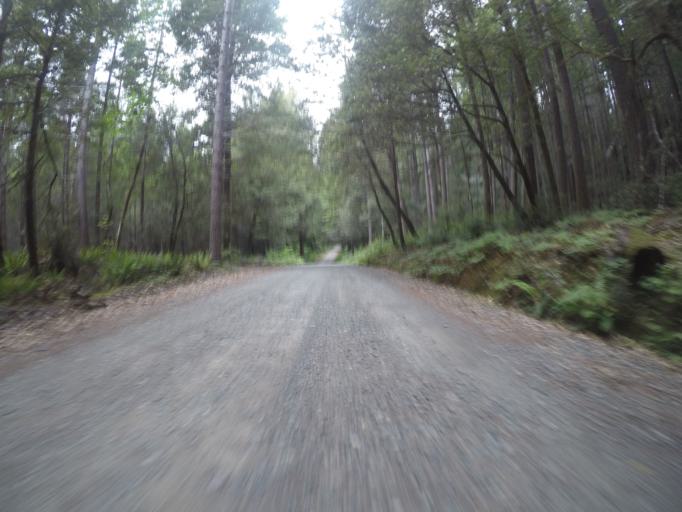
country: US
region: California
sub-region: Del Norte County
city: Bertsch-Oceanview
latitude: 41.7004
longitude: -123.8985
